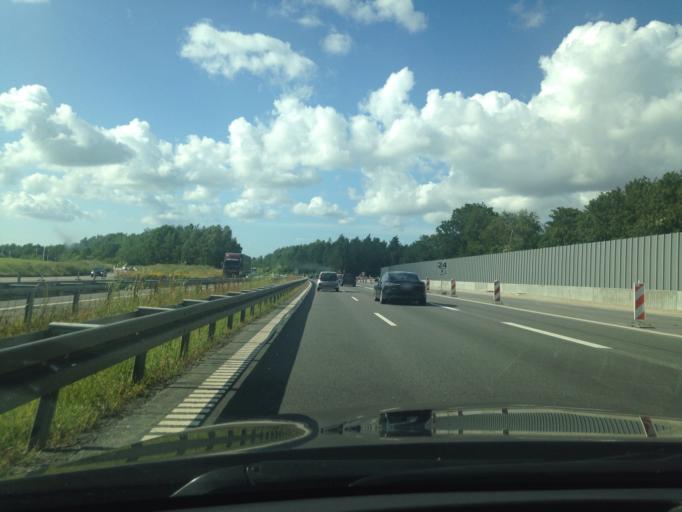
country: DK
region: Capital Region
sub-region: Horsholm Kommune
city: Horsholm
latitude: 55.8560
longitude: 12.4973
